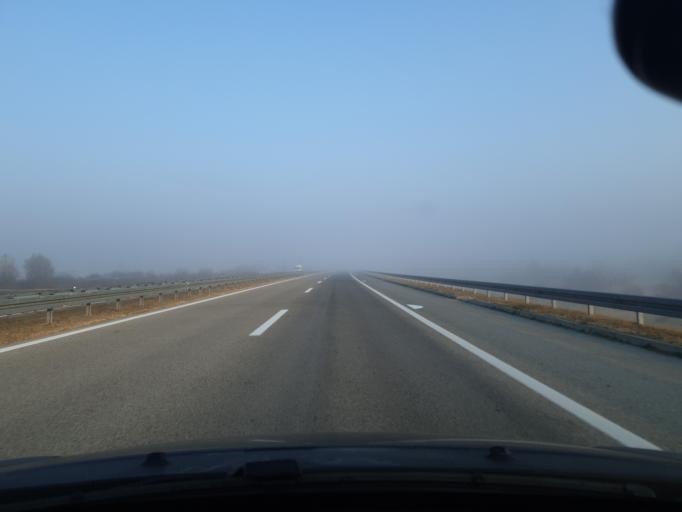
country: RS
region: Central Serbia
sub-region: Jablanicki Okrug
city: Leskovac
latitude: 42.9993
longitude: 22.0251
